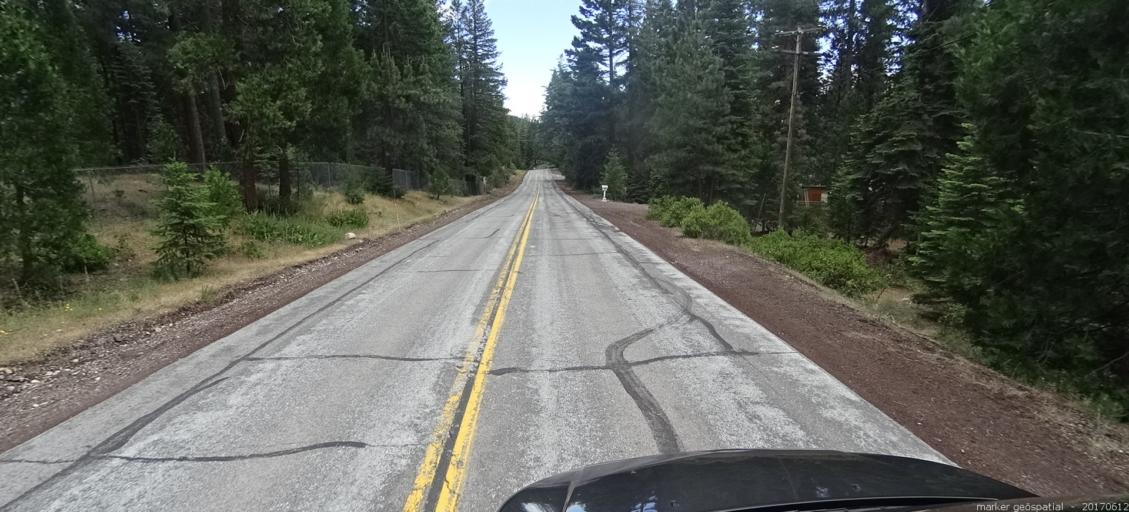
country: US
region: California
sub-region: Siskiyou County
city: Mount Shasta
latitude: 41.3499
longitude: -122.3541
